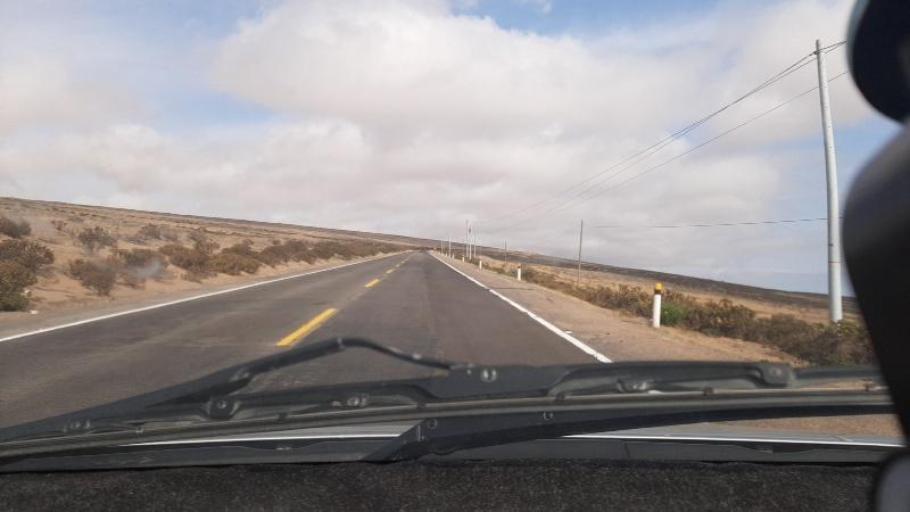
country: PE
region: Moquegua
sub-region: Provincia de Ilo
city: El Algarrobal
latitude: -17.6880
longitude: -71.2766
